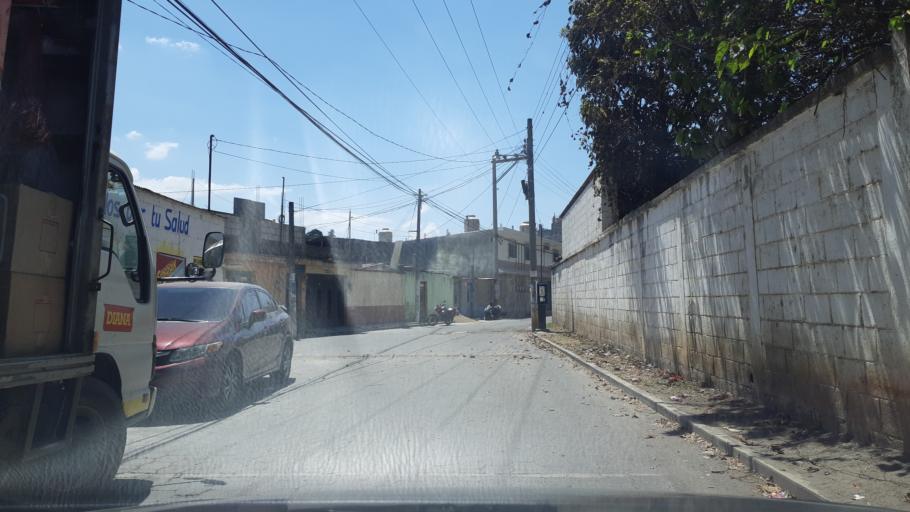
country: GT
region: Chimaltenango
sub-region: Municipio de Chimaltenango
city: Chimaltenango
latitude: 14.6533
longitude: -90.8120
